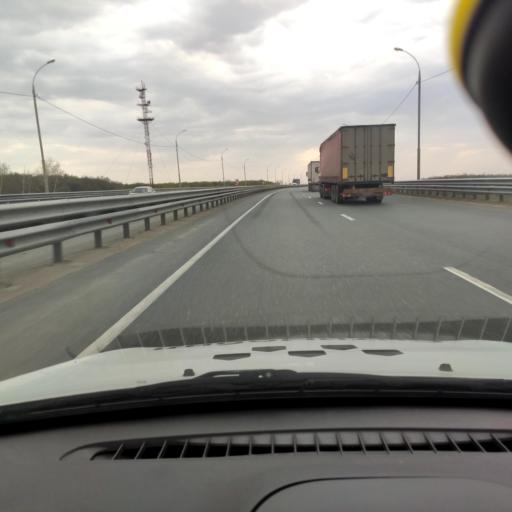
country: RU
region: Samara
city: Mezhdurechensk
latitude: 53.2797
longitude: 49.3190
